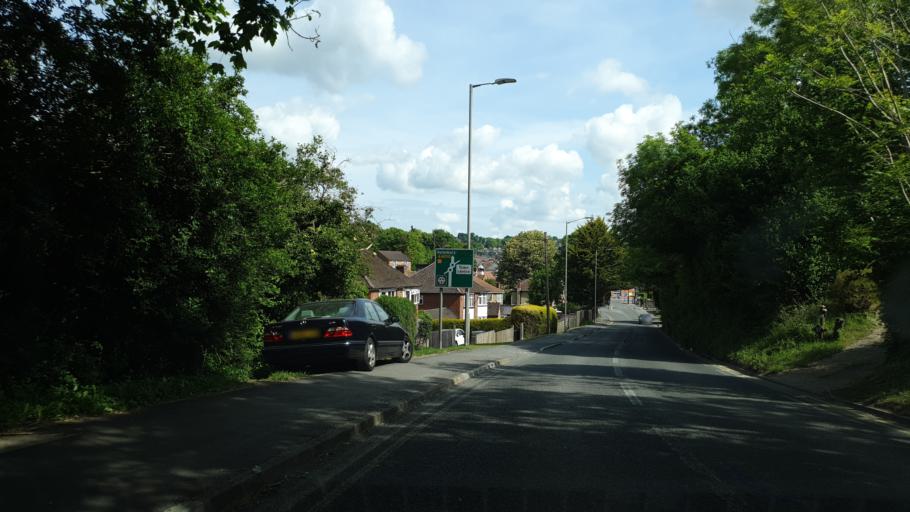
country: GB
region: England
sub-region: Buckinghamshire
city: High Wycombe
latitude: 51.6308
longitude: -0.7854
